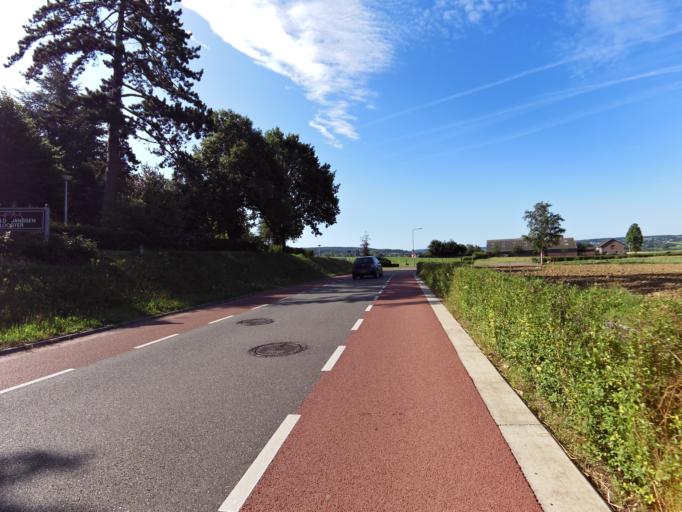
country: NL
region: Limburg
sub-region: Gemeente Voerendaal
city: Ubachsberg
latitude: 50.8058
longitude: 5.9340
